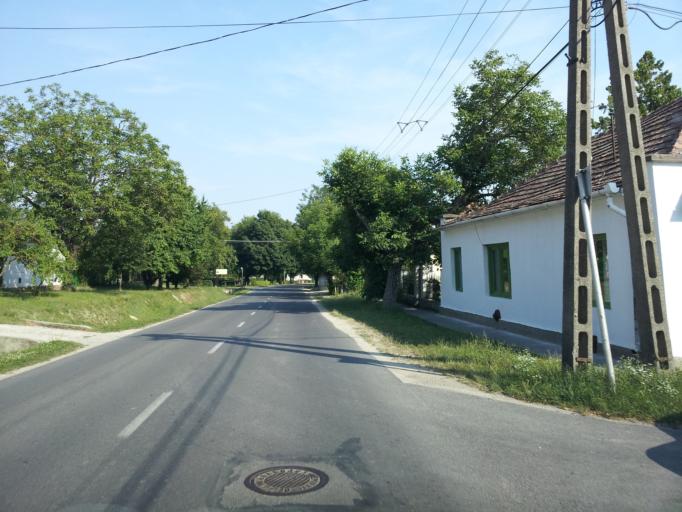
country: HU
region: Veszprem
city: Balatonkenese
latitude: 47.0386
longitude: 18.1060
